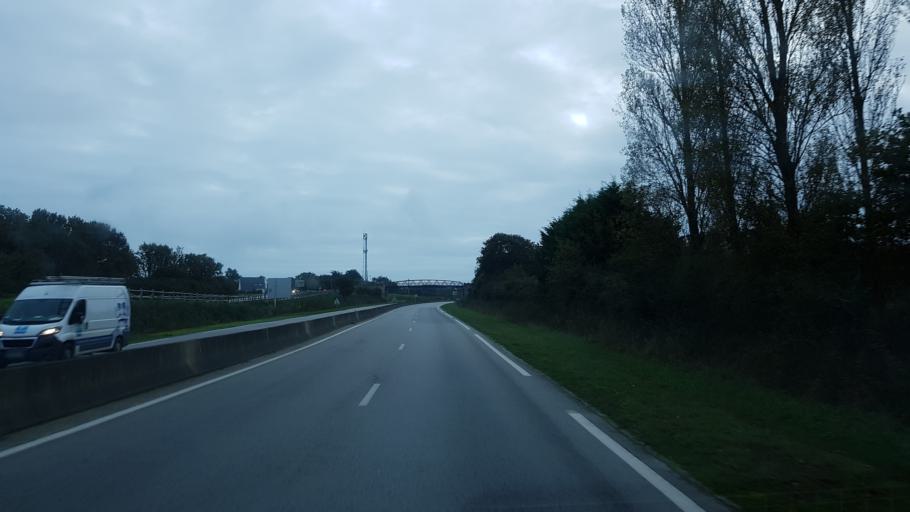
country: FR
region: Brittany
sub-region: Departement du Morbihan
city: Sarzeau
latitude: 47.5499
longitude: -2.7181
